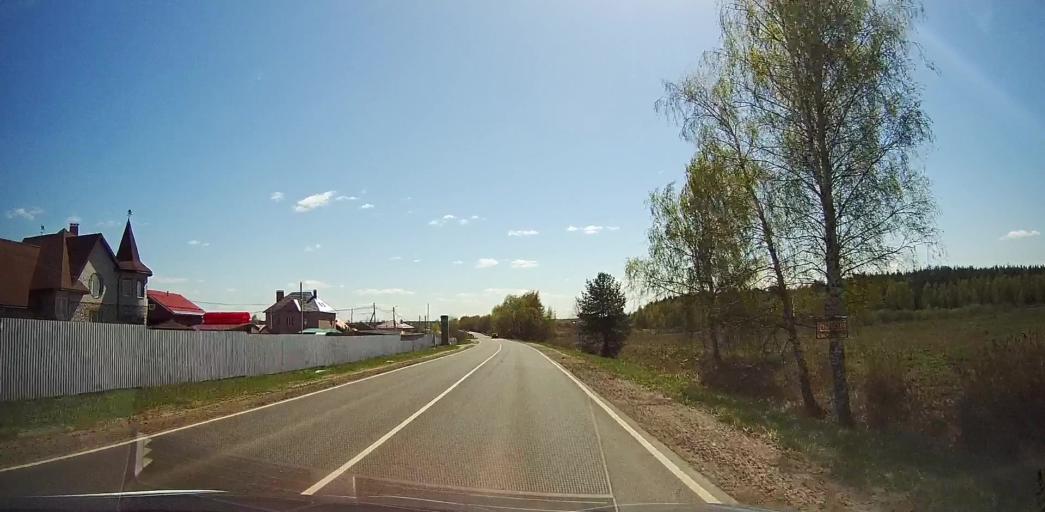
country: RU
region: Moskovskaya
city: Beloozerskiy
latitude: 55.5320
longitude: 38.4288
